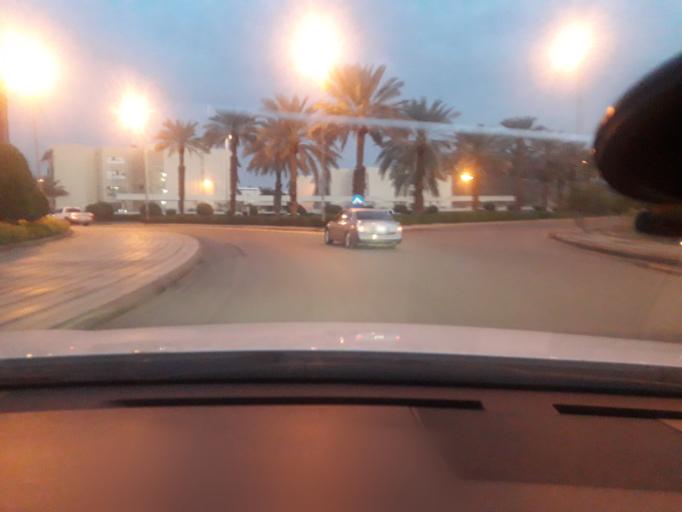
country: SA
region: Al Madinah al Munawwarah
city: Sultanah
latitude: 24.4922
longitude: 39.5852
